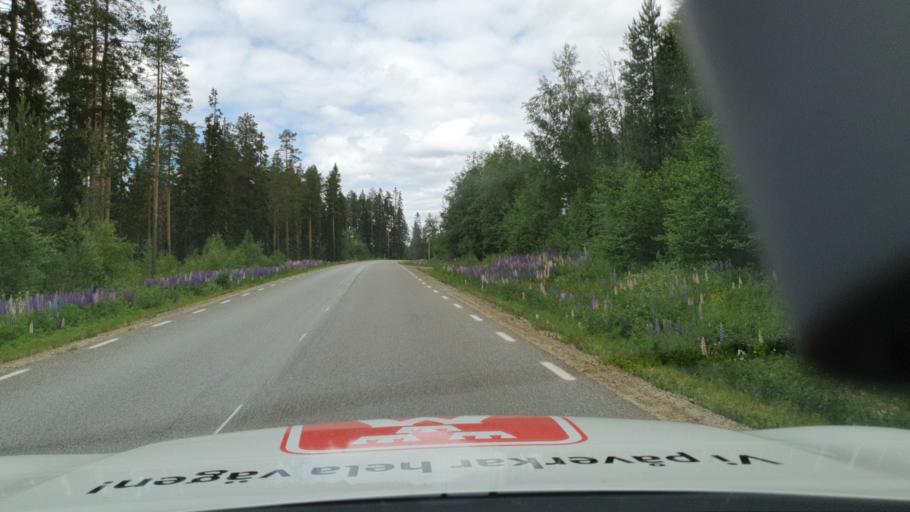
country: SE
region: Vaesterbotten
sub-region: Bjurholms Kommun
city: Bjurholm
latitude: 63.8739
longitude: 18.9840
